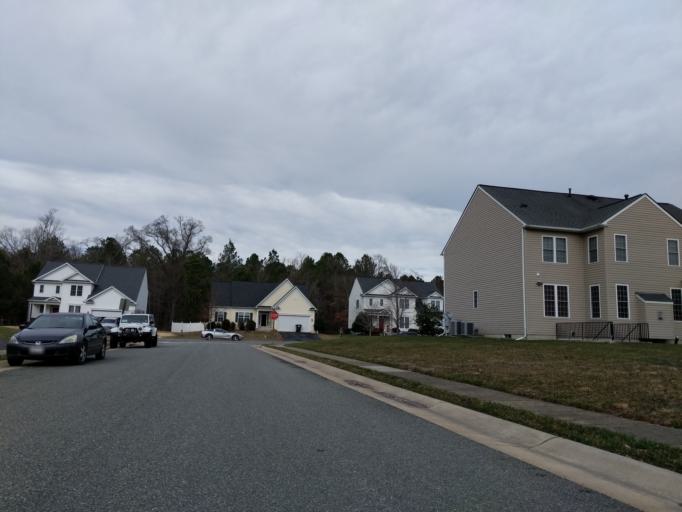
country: US
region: Virginia
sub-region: King George County
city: Dahlgren
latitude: 38.3569
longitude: -77.0594
